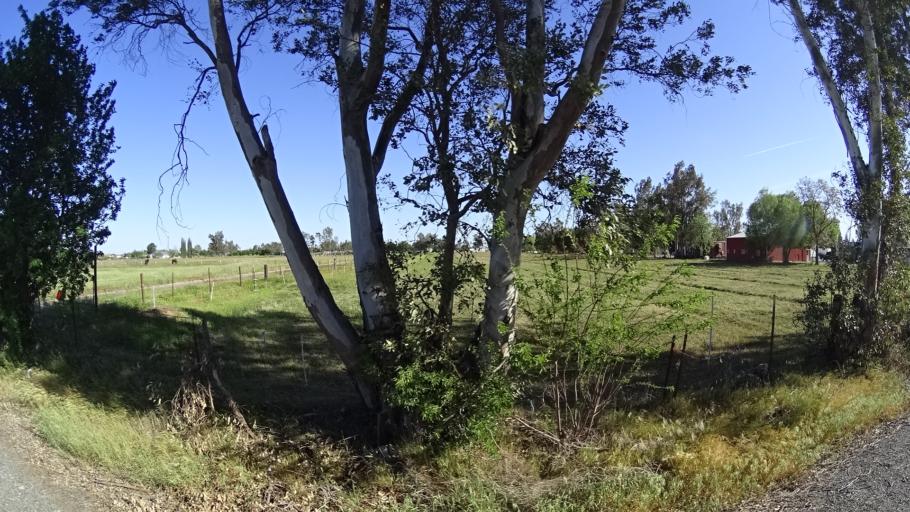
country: US
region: California
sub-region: Glenn County
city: Orland
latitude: 39.7258
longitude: -122.2093
